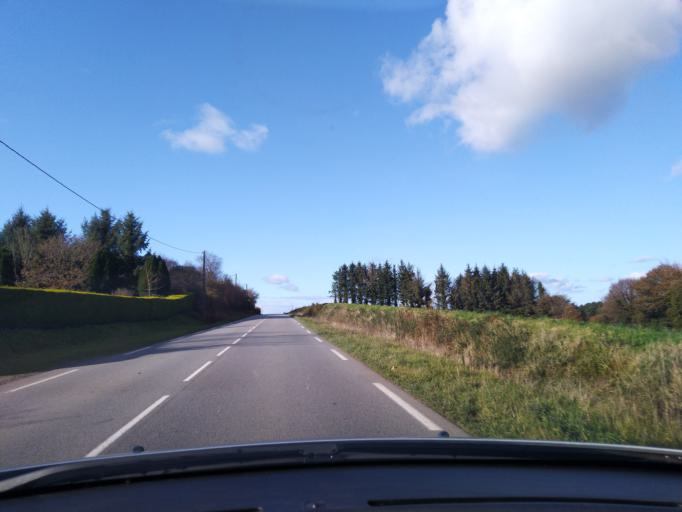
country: FR
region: Brittany
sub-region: Departement du Finistere
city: Guerlesquin
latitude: 48.5257
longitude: -3.5943
